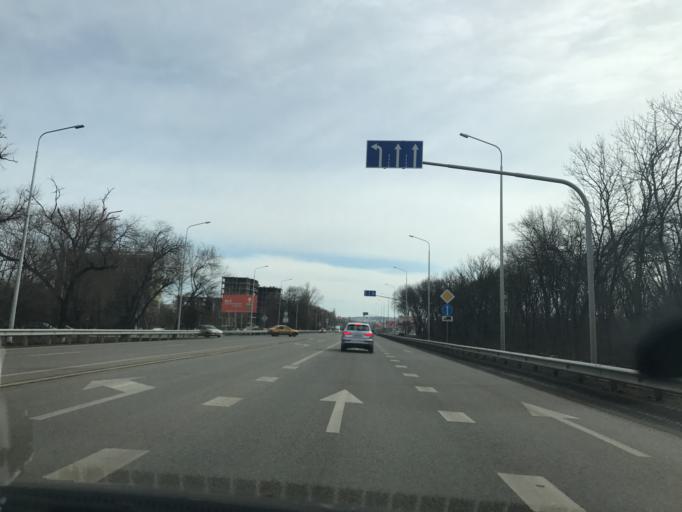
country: RU
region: Stavropol'skiy
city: Mineralnye Vody
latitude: 44.2009
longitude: 43.1146
